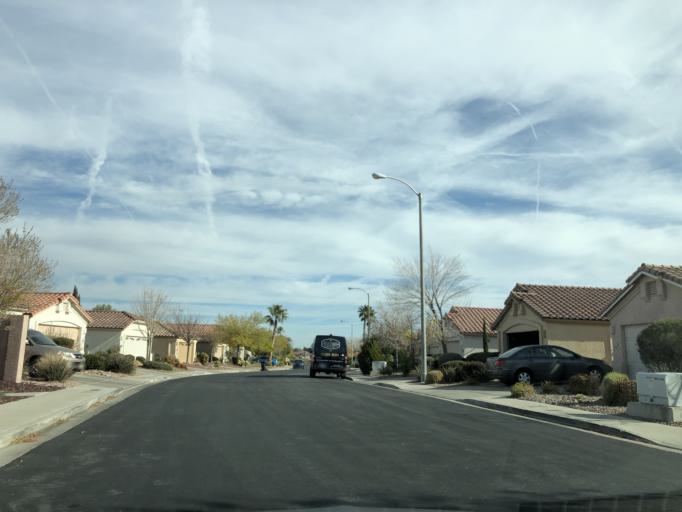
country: US
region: Nevada
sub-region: Clark County
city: Whitney
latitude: 36.0165
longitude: -115.0904
